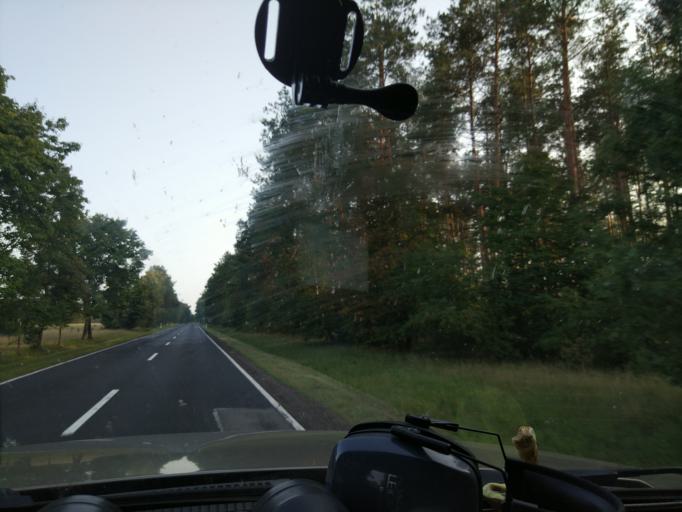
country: PL
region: Warmian-Masurian Voivodeship
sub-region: Powiat szczycienski
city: Wielbark
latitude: 53.3390
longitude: 20.9018
